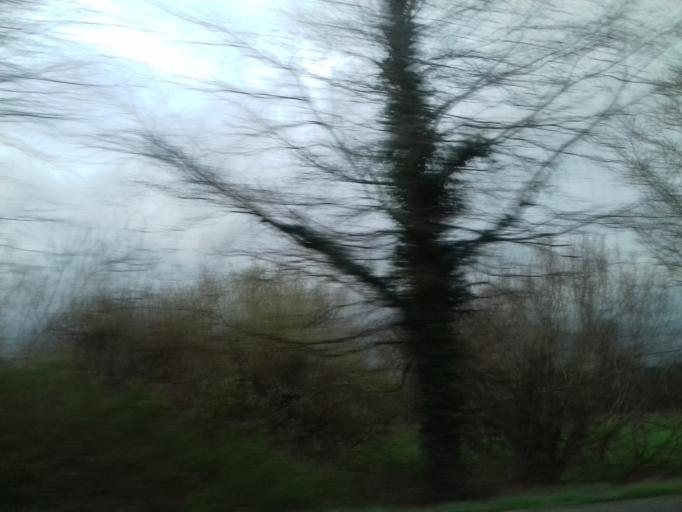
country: IE
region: Munster
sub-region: County Limerick
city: Newcastle West
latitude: 52.4390
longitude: -9.0877
